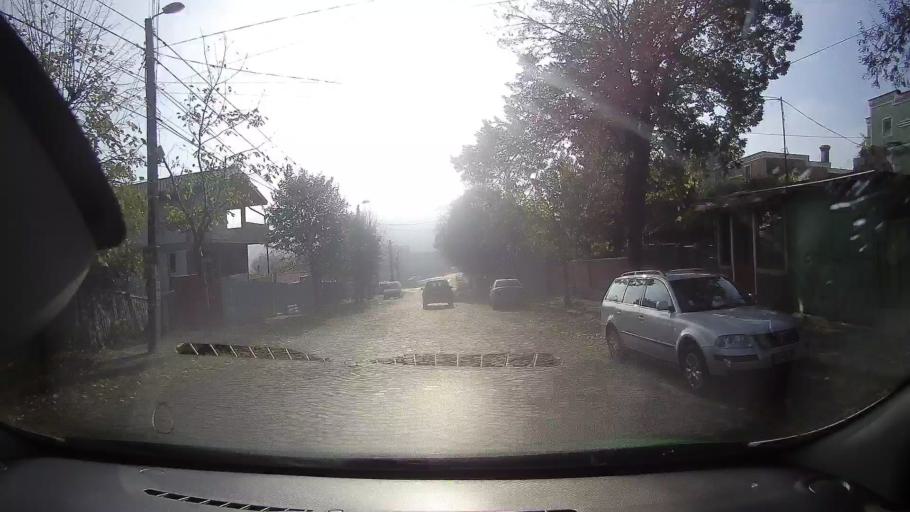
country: RO
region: Tulcea
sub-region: Municipiul Tulcea
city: Tulcea
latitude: 45.1664
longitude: 28.8160
